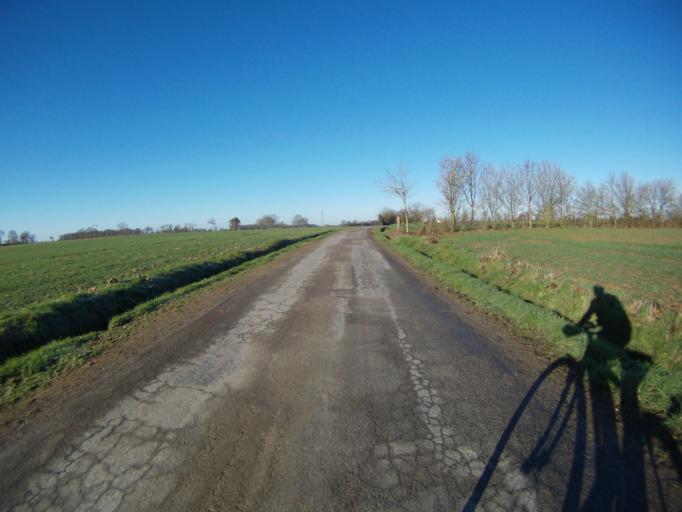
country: FR
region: Brittany
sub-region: Departement d'Ille-et-Vilaine
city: Chanteloup
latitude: 47.9385
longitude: -1.6228
